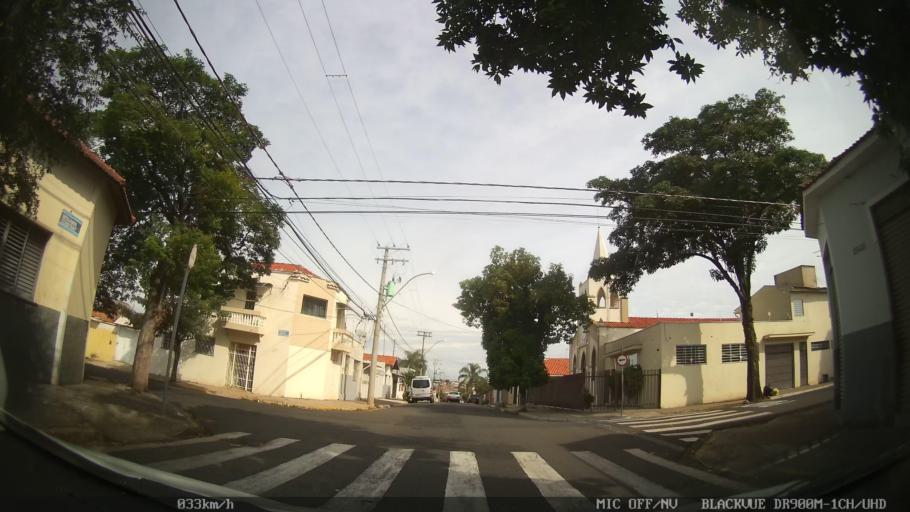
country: BR
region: Sao Paulo
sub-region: Piracicaba
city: Piracicaba
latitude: -22.7428
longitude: -47.6552
